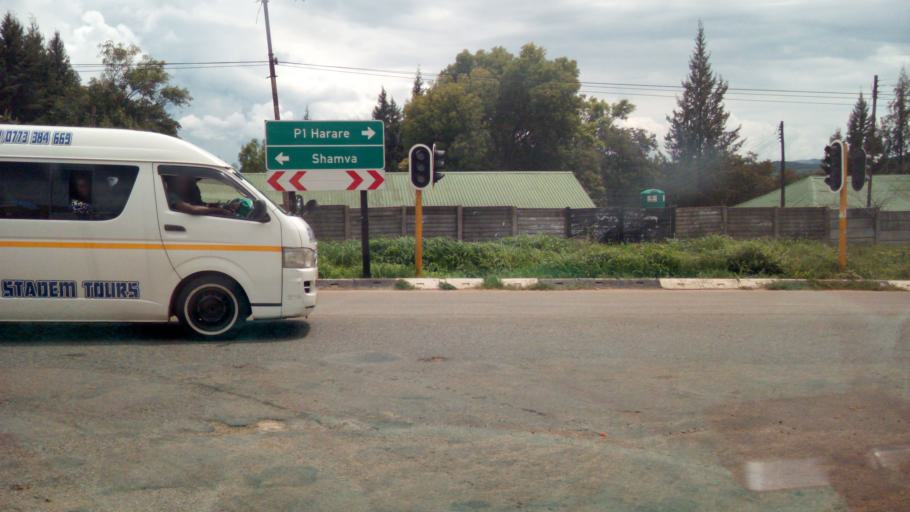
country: ZW
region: Mashonaland Central
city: Bindura
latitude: -17.3041
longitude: 31.3274
